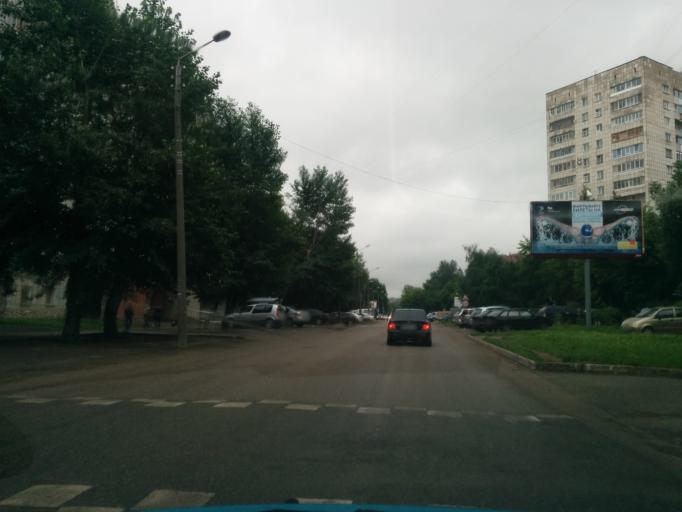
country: RU
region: Perm
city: Perm
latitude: 57.9942
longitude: 56.2287
